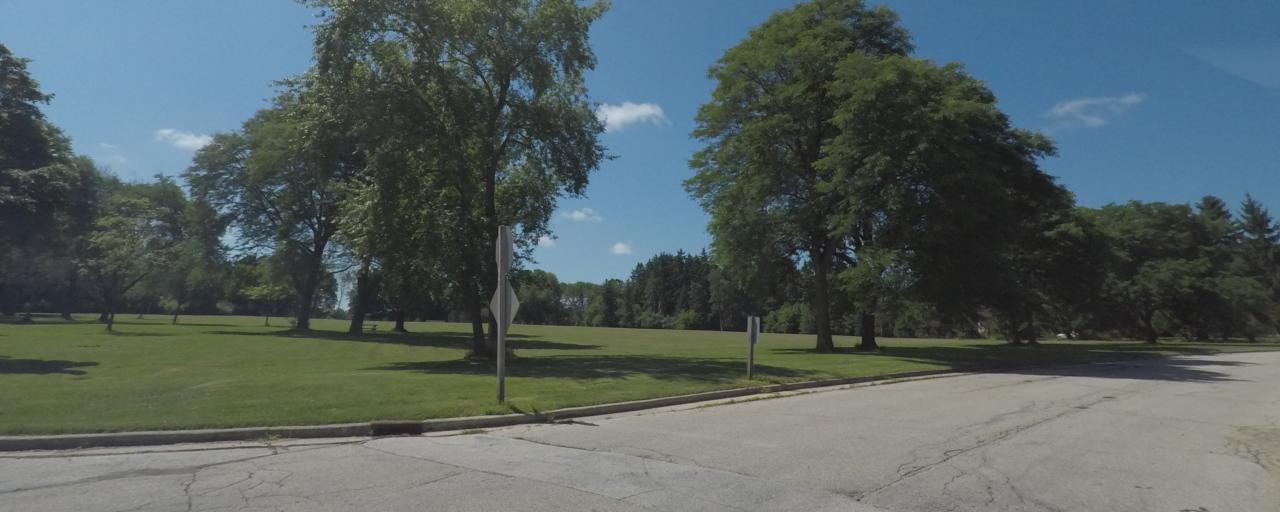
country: US
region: Wisconsin
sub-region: Waukesha County
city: Elm Grove
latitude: 43.0082
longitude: -88.0660
